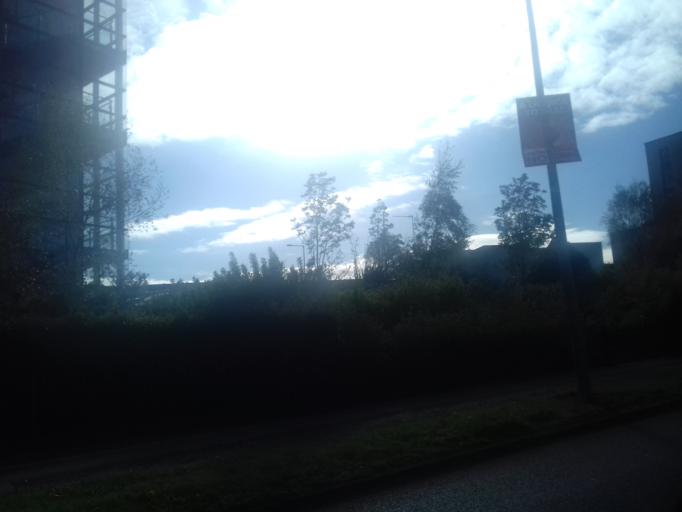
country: IE
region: Leinster
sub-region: Dublin City
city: Finglas
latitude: 53.3817
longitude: -6.2909
